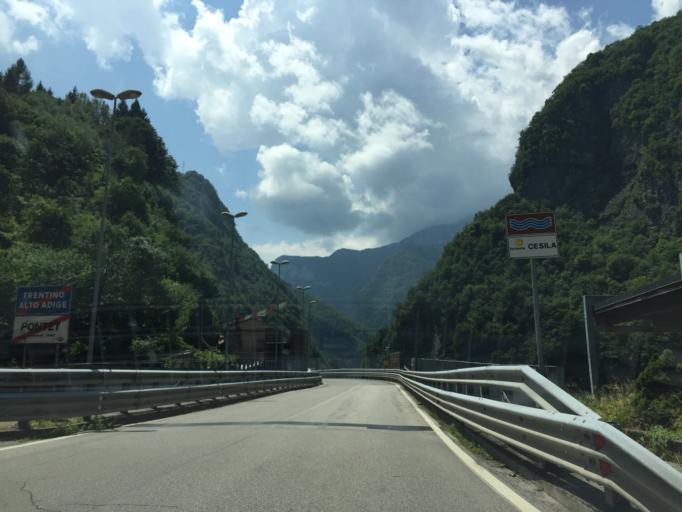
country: IT
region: Trentino-Alto Adige
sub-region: Provincia di Trento
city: Imer
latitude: 46.1066
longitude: 11.7739
